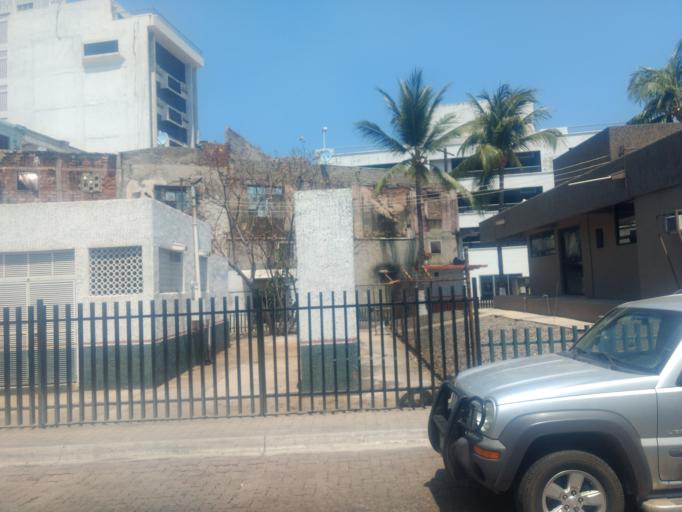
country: MX
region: Colima
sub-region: Manzanillo
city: Manzanillo
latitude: 19.0529
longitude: -104.3139
